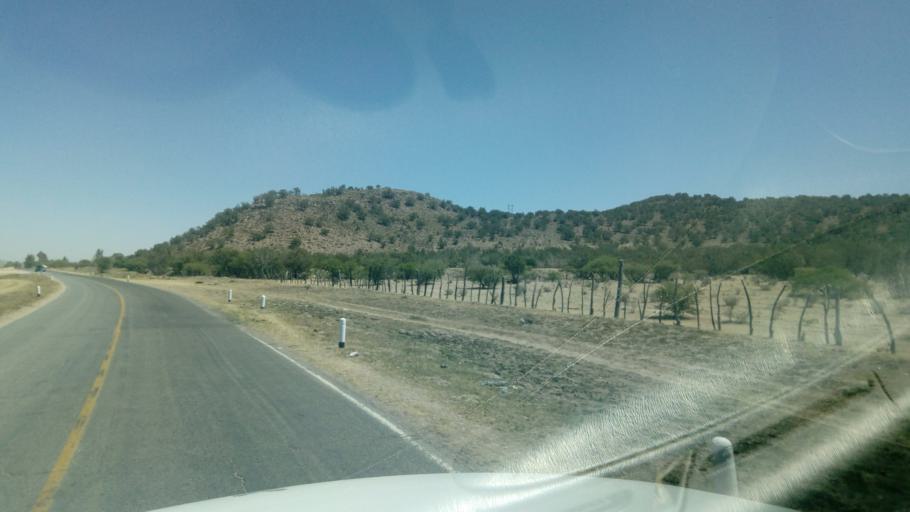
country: MX
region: Durango
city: Victoria de Durango
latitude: 24.1610
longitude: -104.7037
